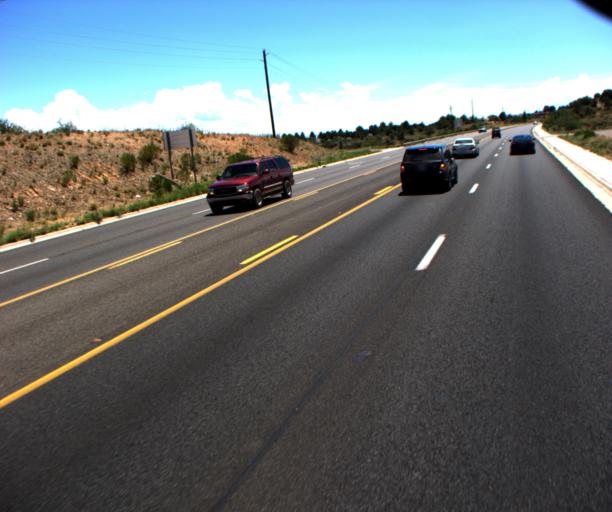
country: US
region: Arizona
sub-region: Yavapai County
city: Verde Village
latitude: 34.7085
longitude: -111.9943
